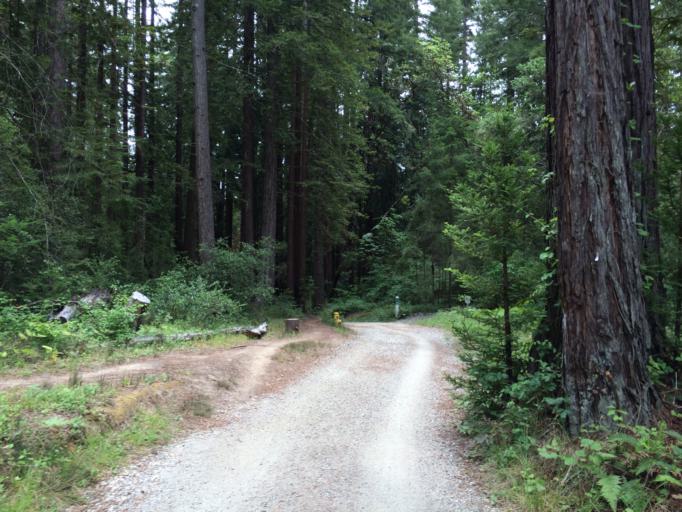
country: US
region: California
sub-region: Santa Cruz County
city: Felton
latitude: 37.0149
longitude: -122.0708
